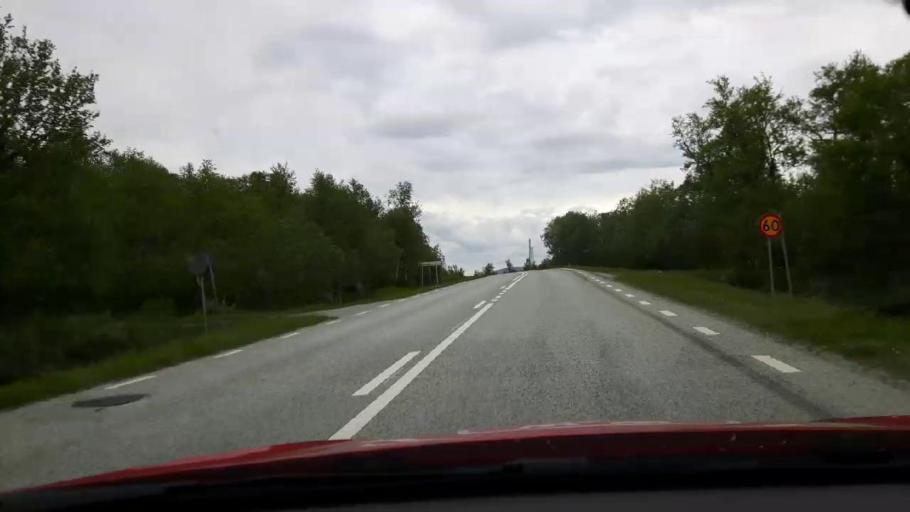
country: NO
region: Sor-Trondelag
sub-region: Tydal
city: Aas
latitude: 62.5716
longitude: 12.2331
